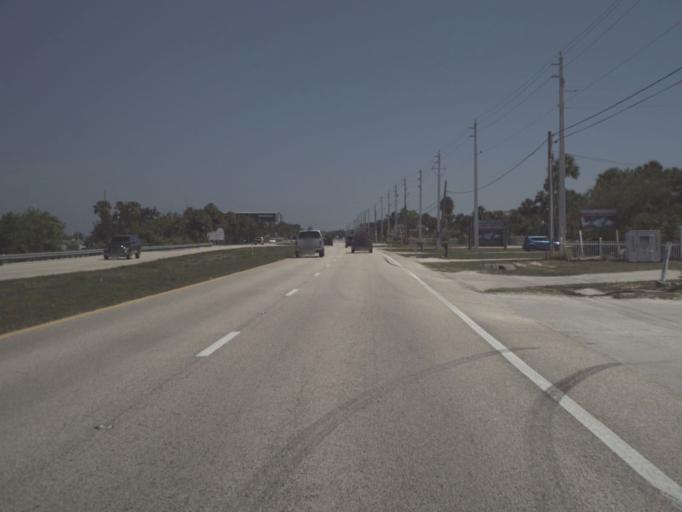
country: US
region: Florida
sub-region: Brevard County
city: Micco
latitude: 27.8750
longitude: -80.4985
